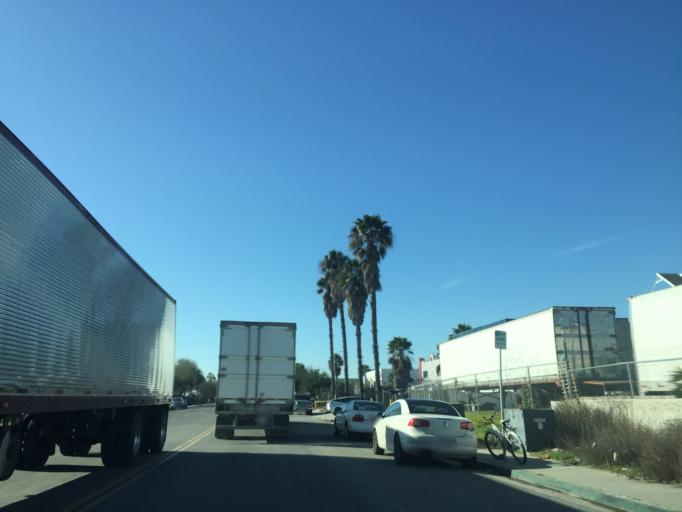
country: MX
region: Baja California
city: Tijuana
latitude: 32.5529
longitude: -116.9323
